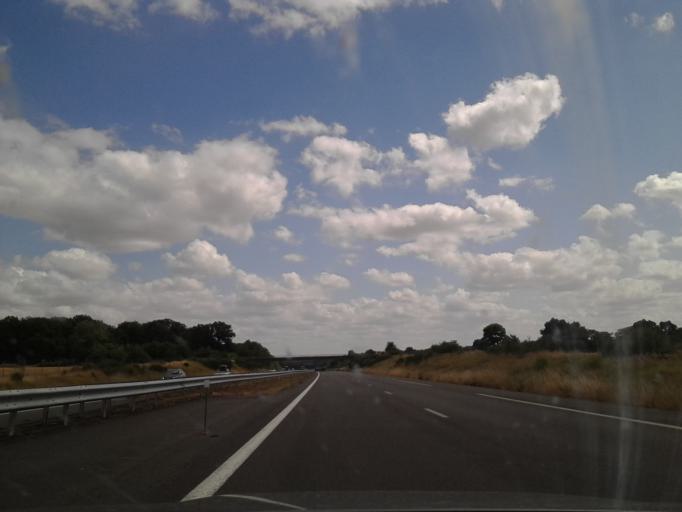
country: FR
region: Centre
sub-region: Departement du Cher
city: Orval
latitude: 46.8052
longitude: 2.4125
